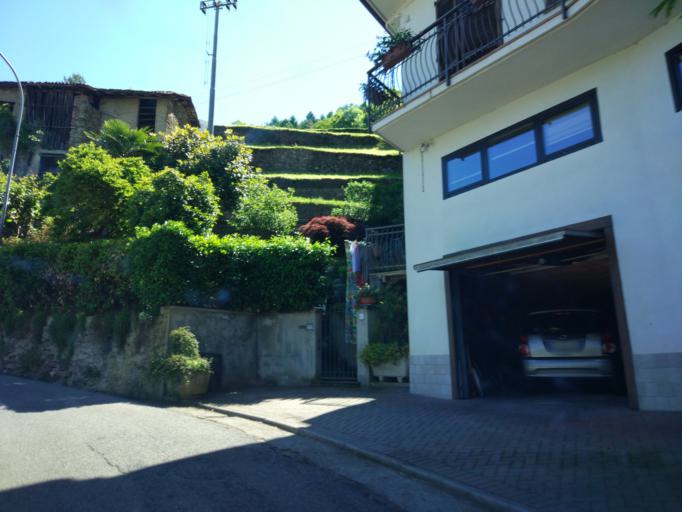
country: IT
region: Lombardy
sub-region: Provincia di Lecco
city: Bellano
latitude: 46.0474
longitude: 9.3128
